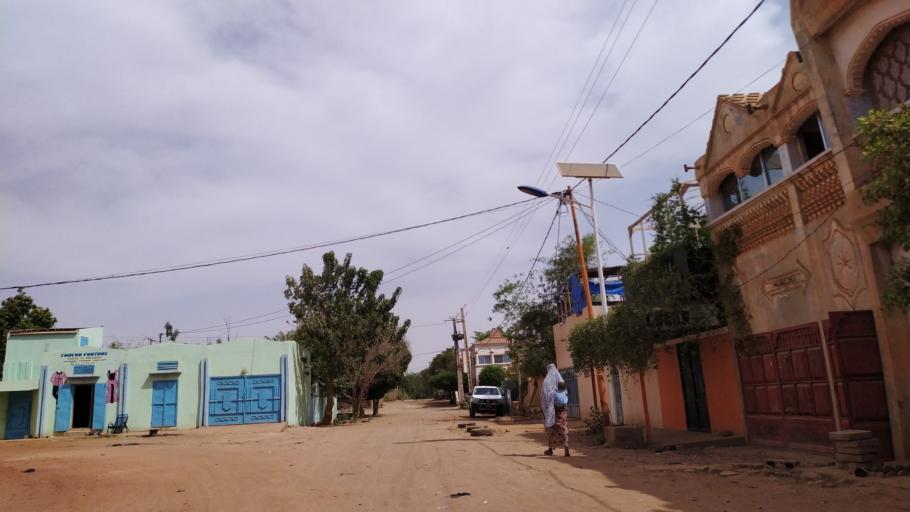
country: ML
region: Kayes
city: Kayes
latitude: 14.4561
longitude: -11.4638
